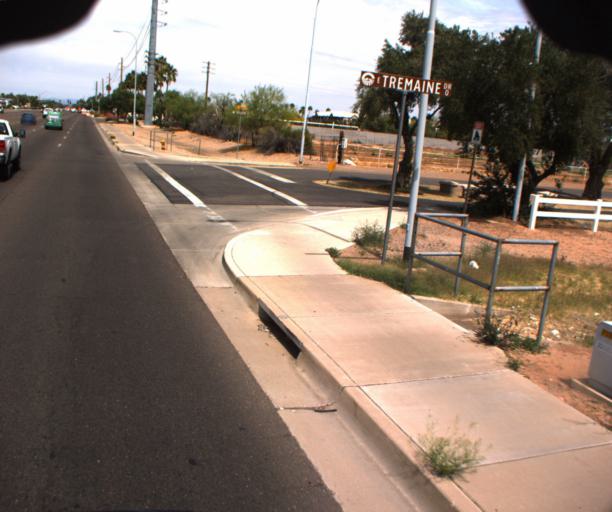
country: US
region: Arizona
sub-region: Maricopa County
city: San Carlos
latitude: 33.3604
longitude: -111.8417
